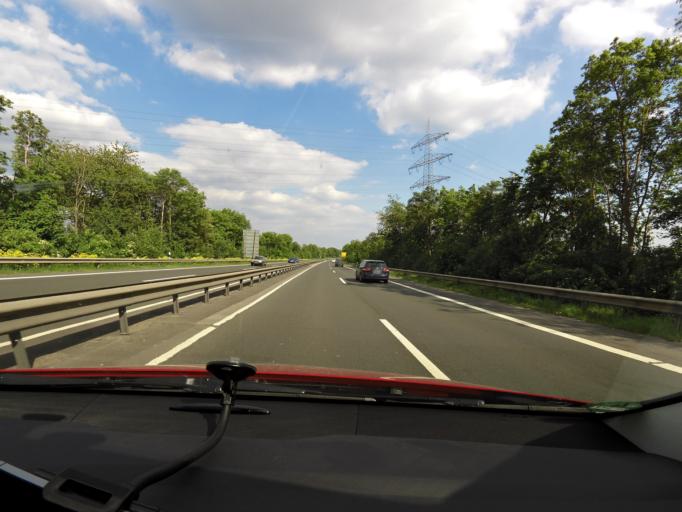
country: DE
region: Rheinland-Pfalz
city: Weissenthurm
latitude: 50.4177
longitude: 7.4259
